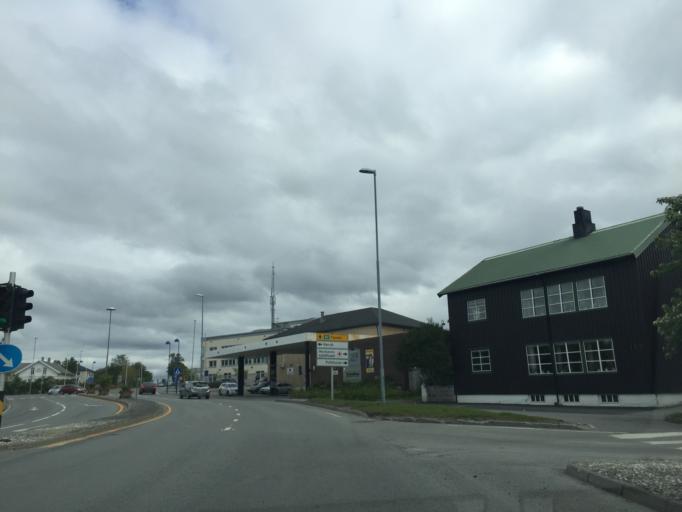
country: NO
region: Nordland
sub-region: Bodo
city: Bodo
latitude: 67.2862
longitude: 14.3988
